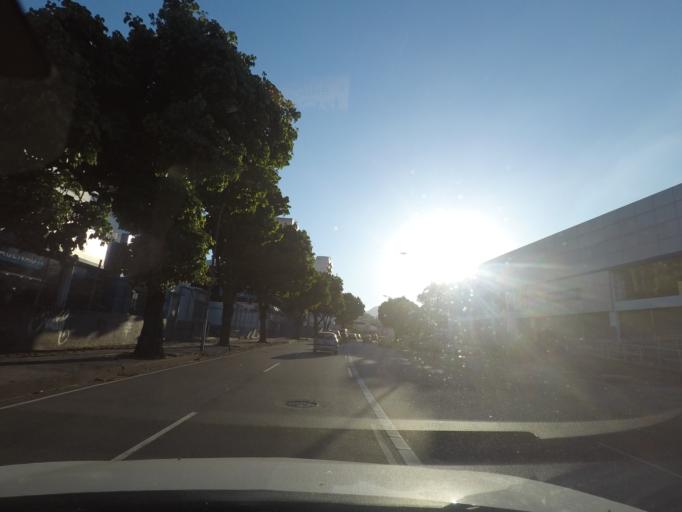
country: BR
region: Rio de Janeiro
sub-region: Rio De Janeiro
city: Rio de Janeiro
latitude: -22.9149
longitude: -43.2081
